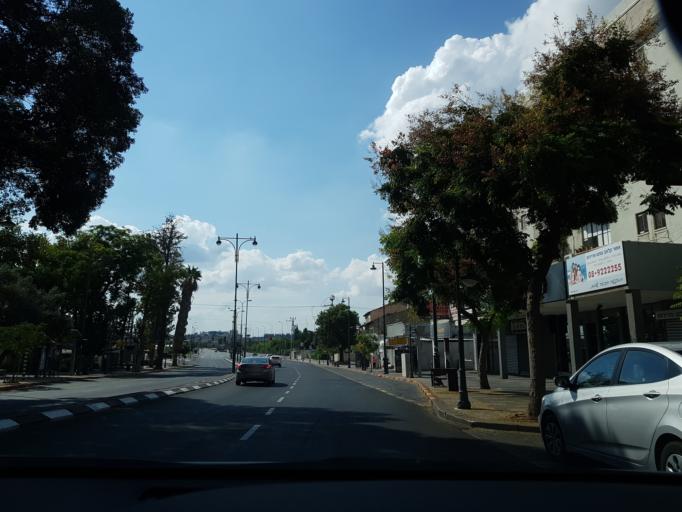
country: IL
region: Central District
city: Ness Ziona
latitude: 31.9261
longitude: 34.7978
